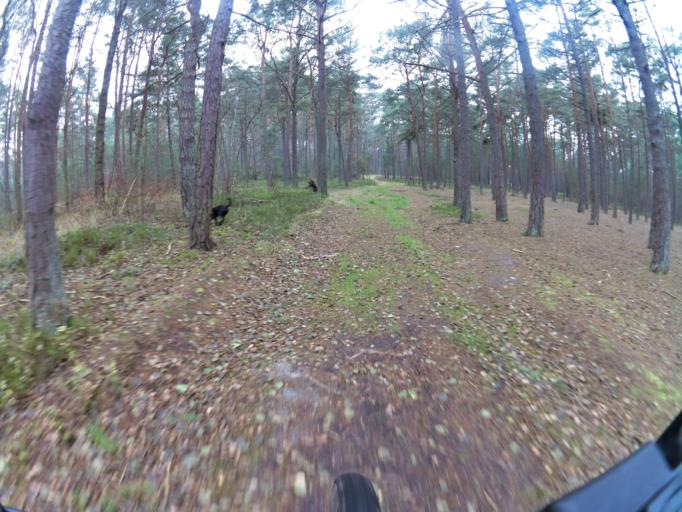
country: PL
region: West Pomeranian Voivodeship
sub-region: Powiat gryficki
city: Cerkwica
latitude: 54.0980
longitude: 15.1308
